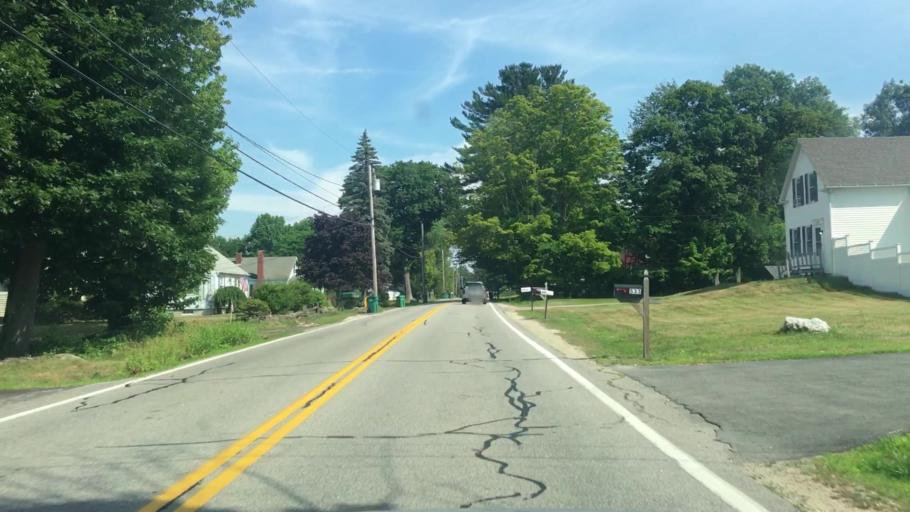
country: US
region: New Hampshire
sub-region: Strafford County
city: Rochester
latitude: 43.3205
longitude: -70.9451
